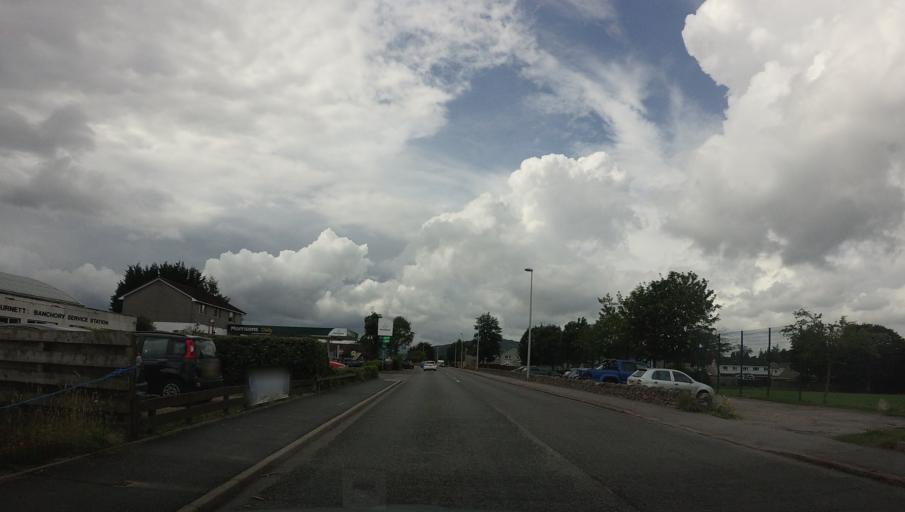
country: GB
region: Scotland
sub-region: Aberdeenshire
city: Banchory
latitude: 57.0548
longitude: -2.4797
